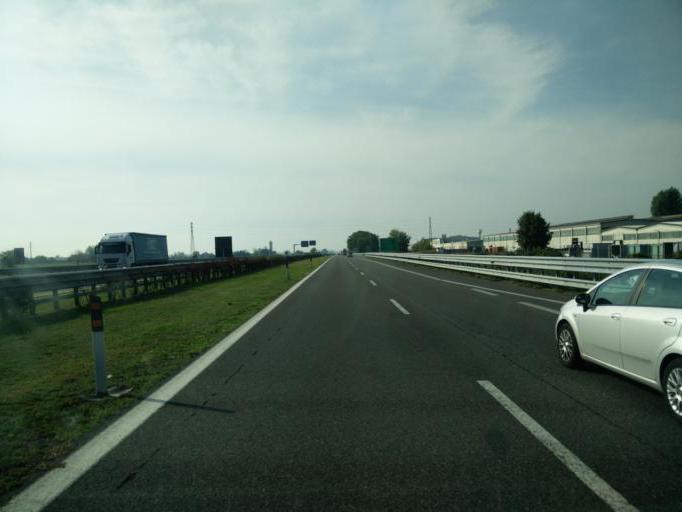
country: IT
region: Lombardy
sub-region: Provincia di Brescia
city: Alfianello
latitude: 45.2684
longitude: 10.1279
